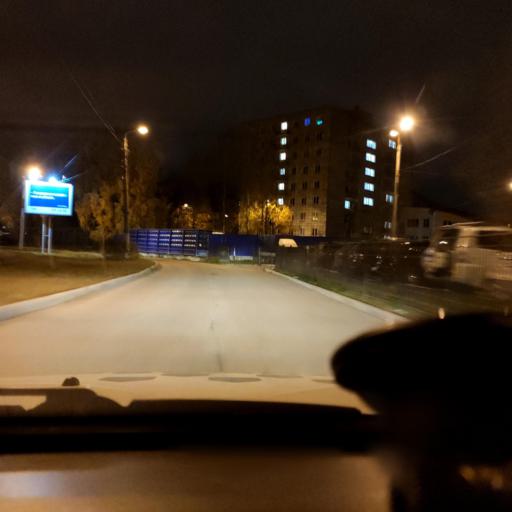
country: RU
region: Perm
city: Perm
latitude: 58.0122
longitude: 56.2795
